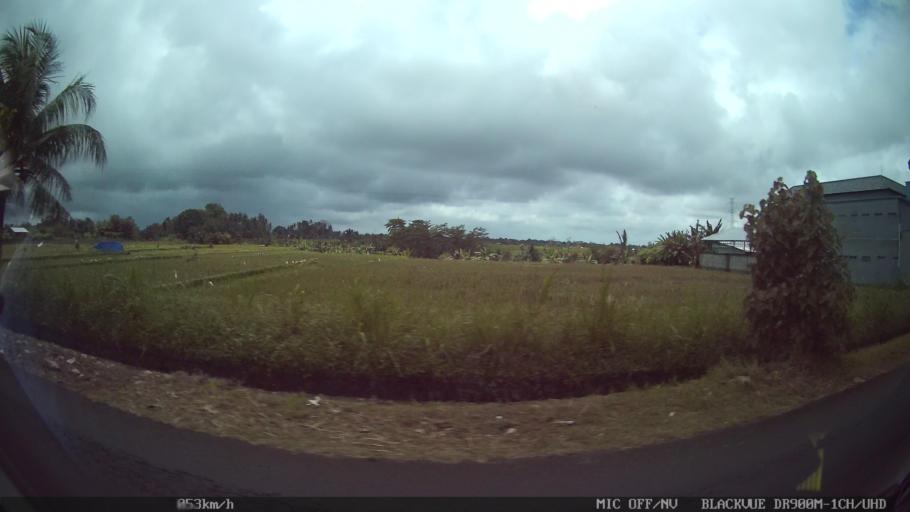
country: ID
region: Bali
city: Banjar Tengahbelayu
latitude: -8.5262
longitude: 115.1810
